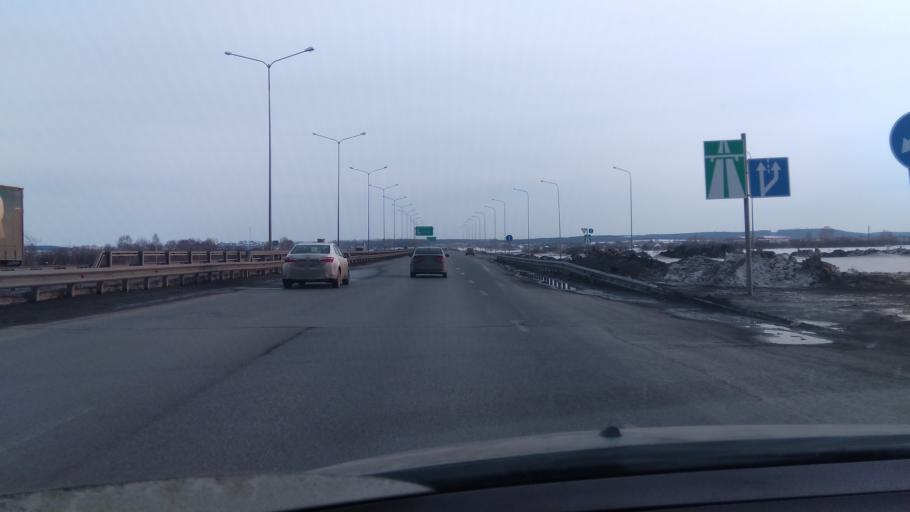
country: RU
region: Perm
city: Froly
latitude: 57.8952
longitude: 56.2657
